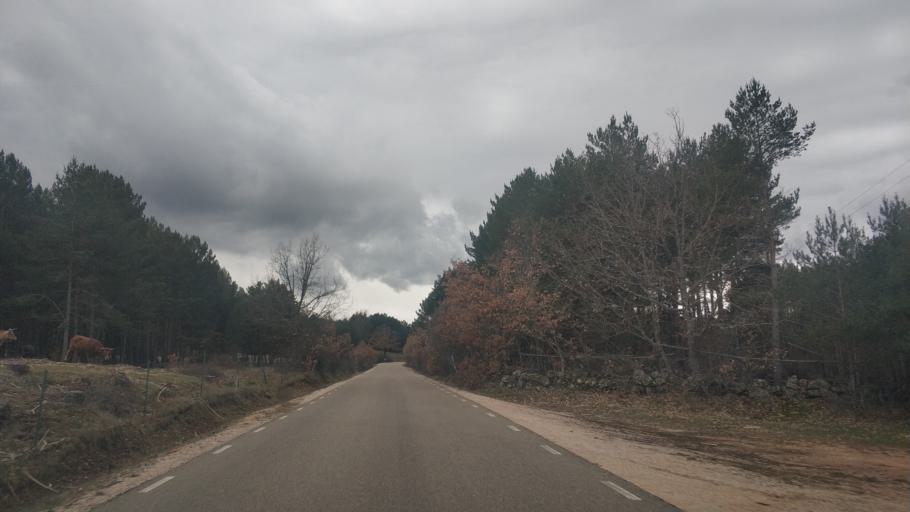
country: ES
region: Castille and Leon
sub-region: Provincia de Burgos
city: Canicosa de la Sierra
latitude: 41.9514
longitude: -3.0237
